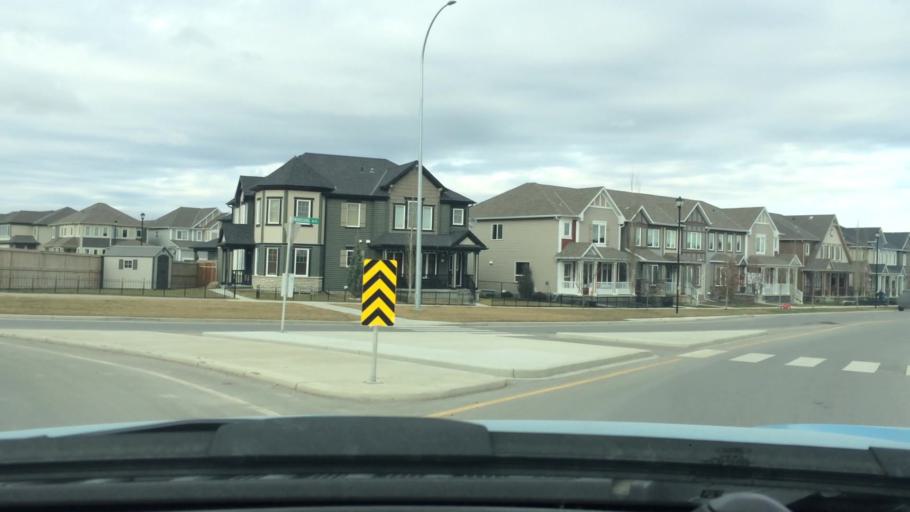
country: CA
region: Alberta
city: Airdrie
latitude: 51.2562
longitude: -114.0321
